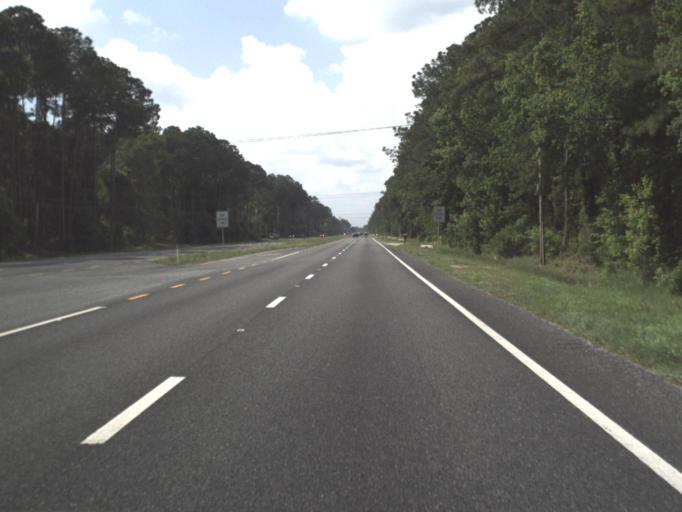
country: US
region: Florida
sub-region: Saint Johns County
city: Saint Augustine Shores
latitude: 29.7713
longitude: -81.3155
